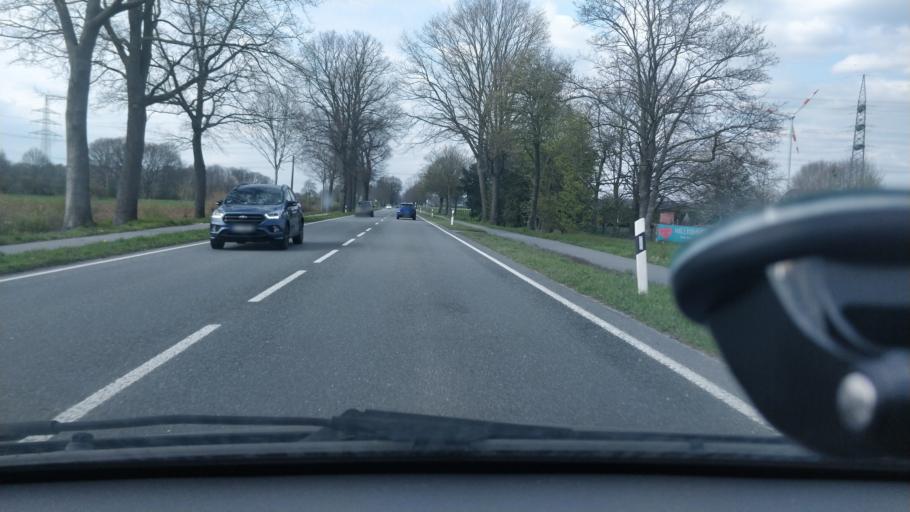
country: DE
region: North Rhine-Westphalia
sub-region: Regierungsbezirk Dusseldorf
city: Wesel
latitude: 51.6974
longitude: 6.6048
